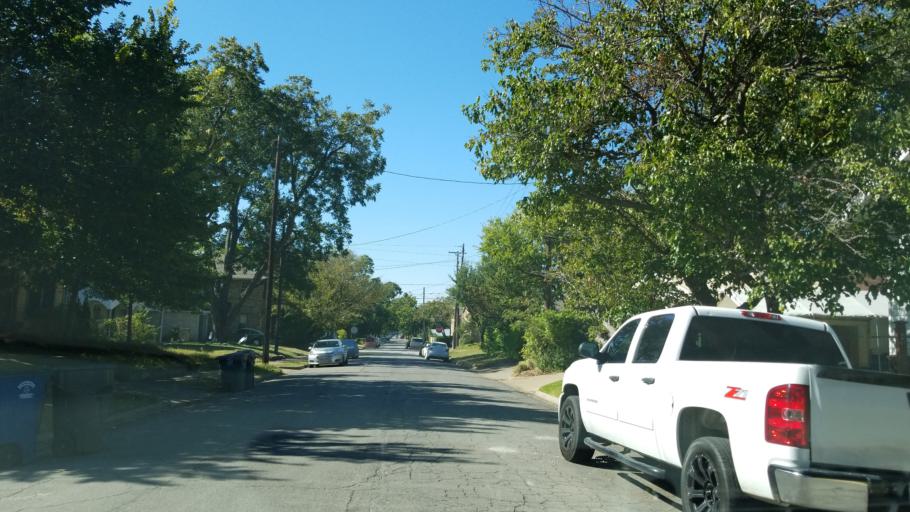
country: US
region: Texas
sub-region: Dallas County
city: Highland Park
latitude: 32.8055
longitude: -96.7600
